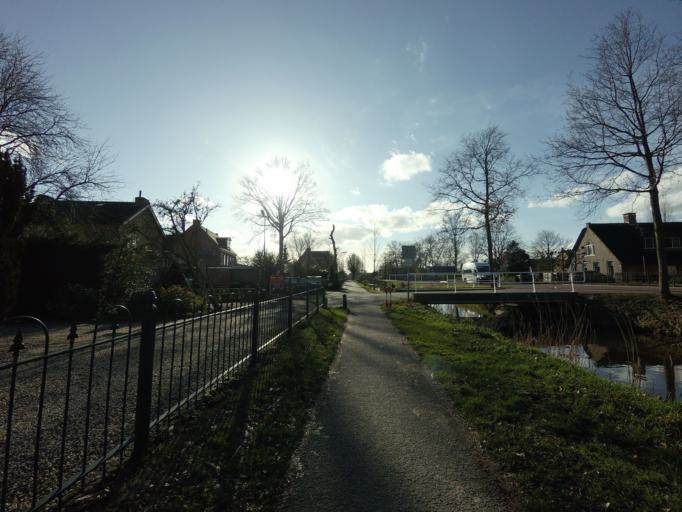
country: NL
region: Utrecht
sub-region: Gemeente IJsselstein
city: IJsselstein
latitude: 51.9921
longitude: 5.0466
